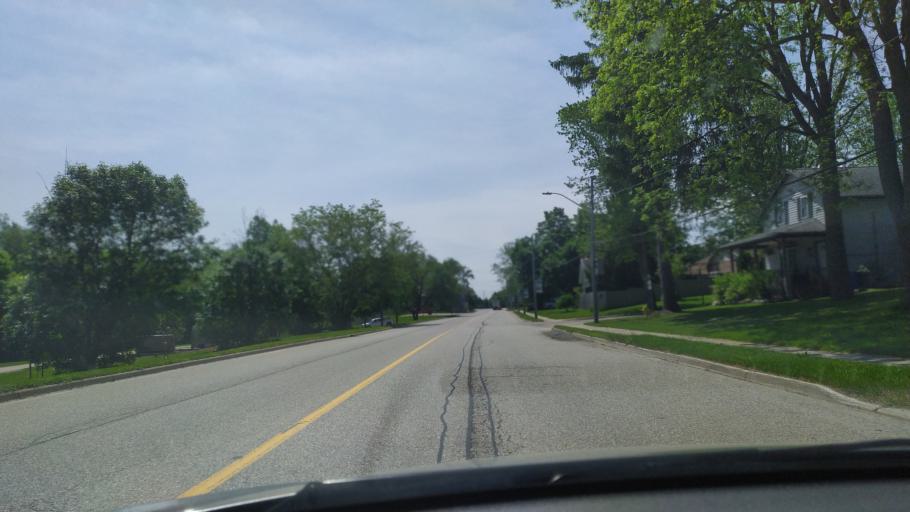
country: CA
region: Ontario
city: Dorchester
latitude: 43.0614
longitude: -80.9976
